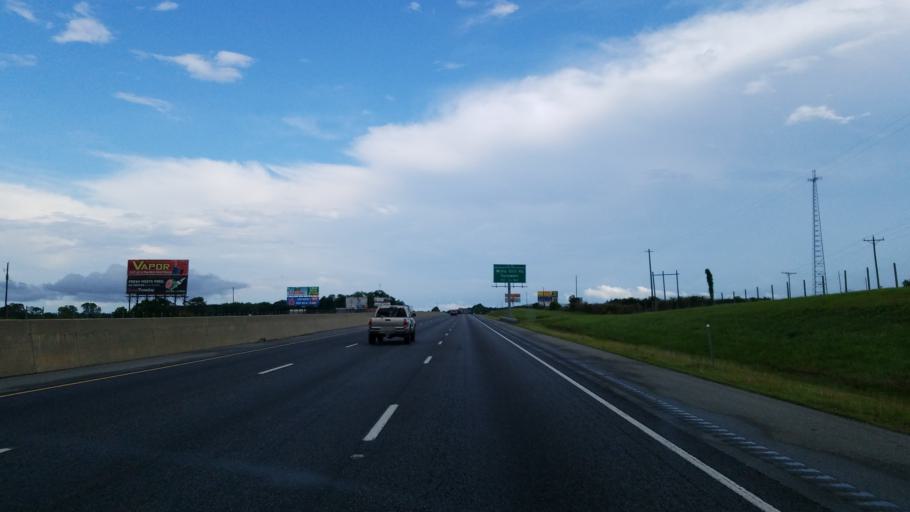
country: US
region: Georgia
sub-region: Tift County
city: Tifton
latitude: 31.5800
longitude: -83.5525
